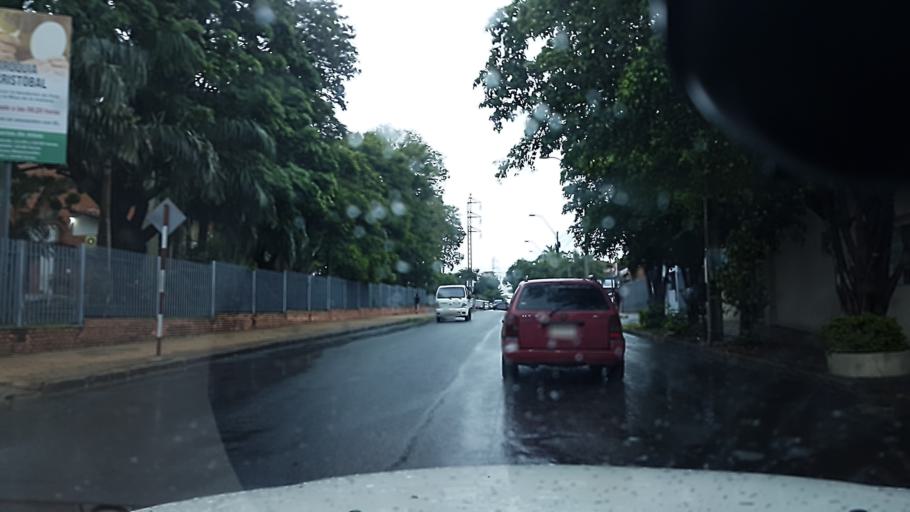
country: PY
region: Central
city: Fernando de la Mora
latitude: -25.2983
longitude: -57.5637
